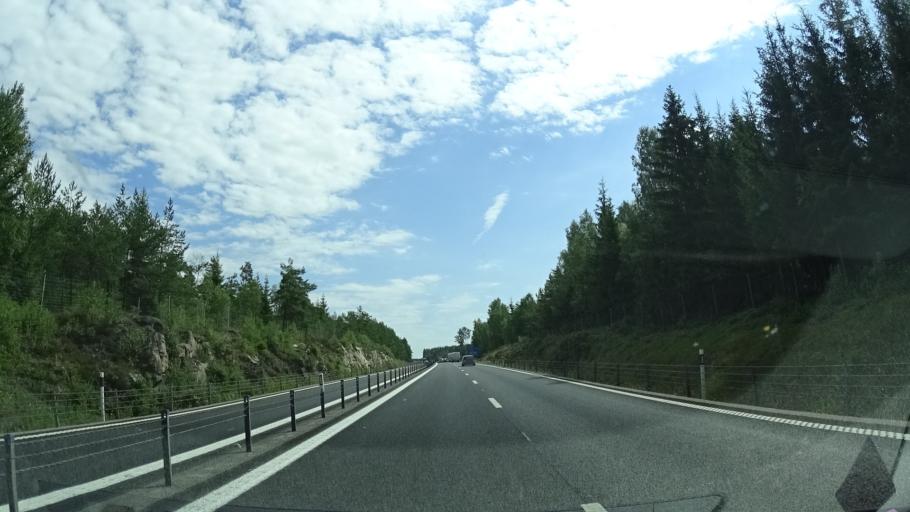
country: SE
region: Vaermland
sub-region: Karlstads Kommun
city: Skattkarr
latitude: 59.3926
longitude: 13.8280
